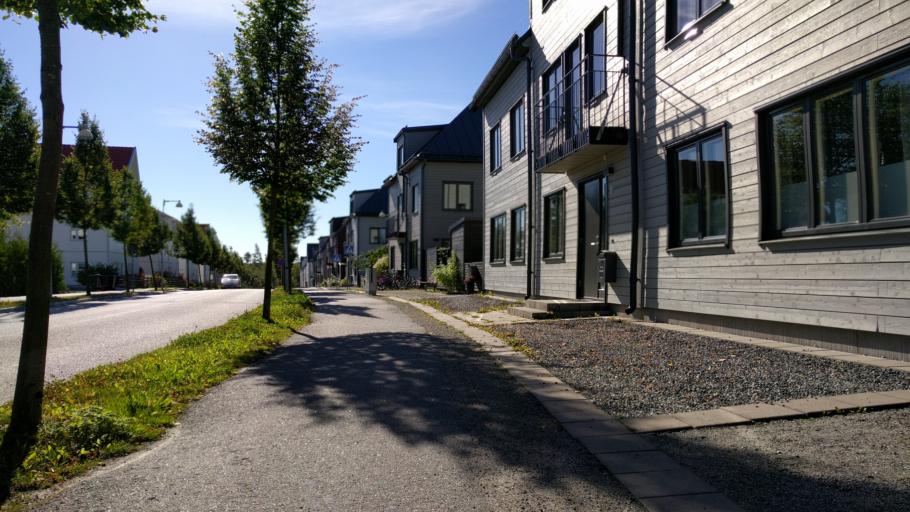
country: SE
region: Stockholm
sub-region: Vallentuna Kommun
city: Vallentuna
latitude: 59.4999
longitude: 18.0886
